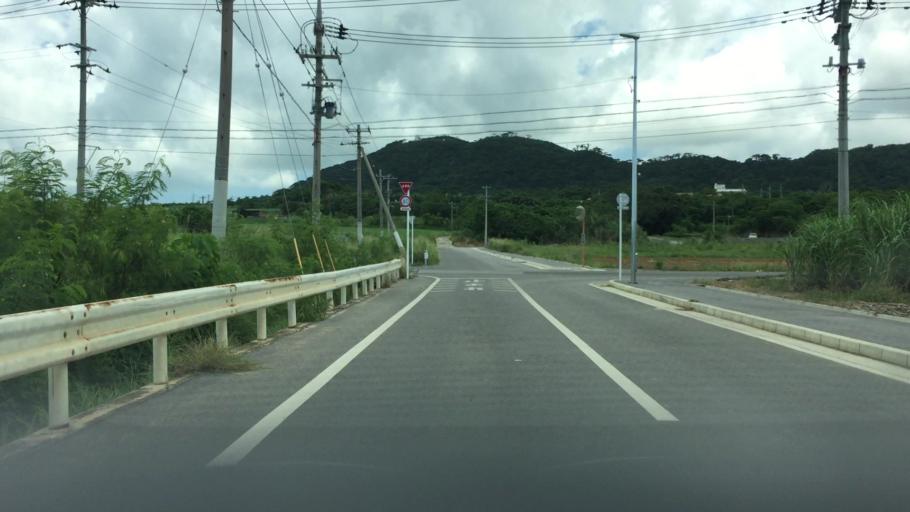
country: JP
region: Okinawa
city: Ishigaki
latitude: 24.3599
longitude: 124.1391
